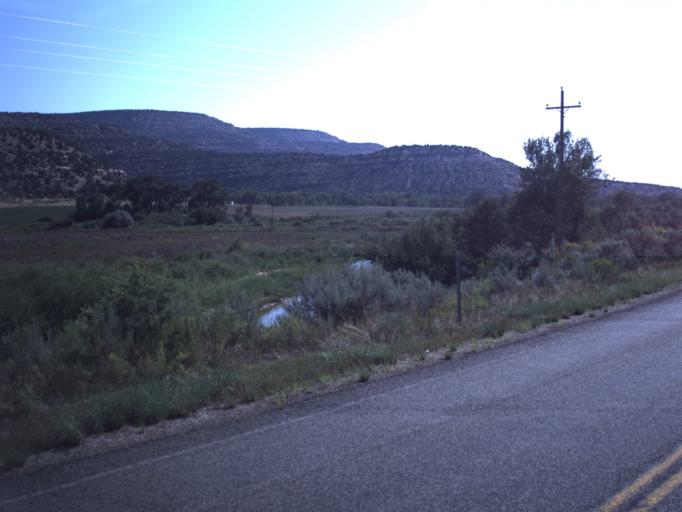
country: US
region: Utah
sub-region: Duchesne County
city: Duchesne
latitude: 40.2931
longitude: -110.5059
